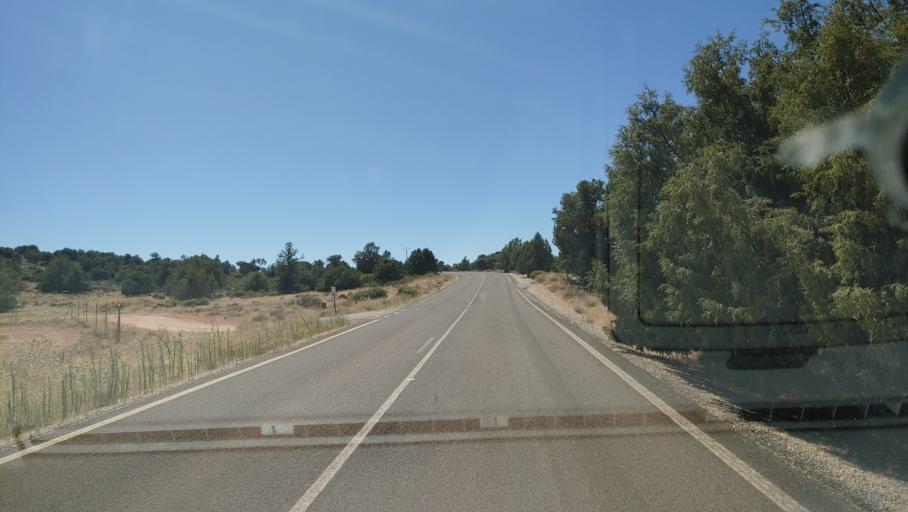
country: ES
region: Castille-La Mancha
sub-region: Provincia de Ciudad Real
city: Villahermosa
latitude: 38.8521
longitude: -2.8053
